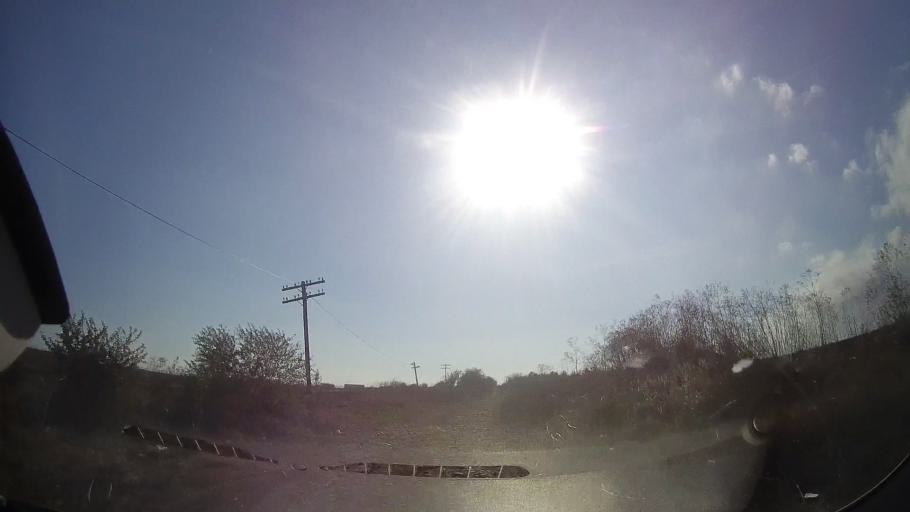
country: RO
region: Constanta
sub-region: Comuna Tuzla
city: Tuzla
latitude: 43.9753
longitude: 28.6441
